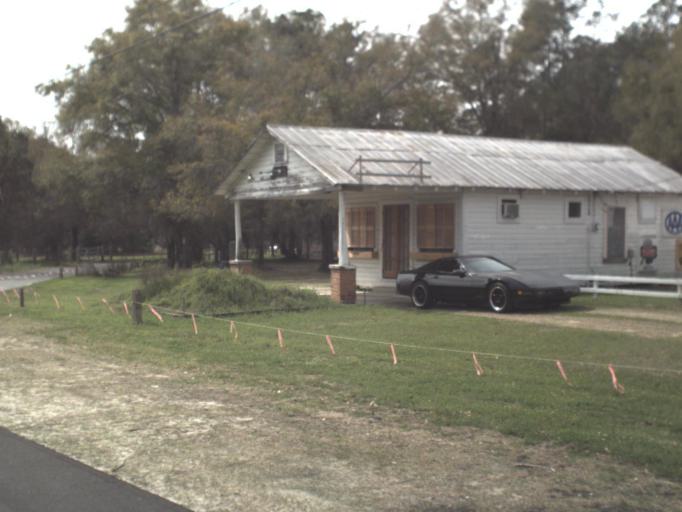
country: US
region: Florida
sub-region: Gadsden County
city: Midway
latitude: 30.4337
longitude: -84.5254
